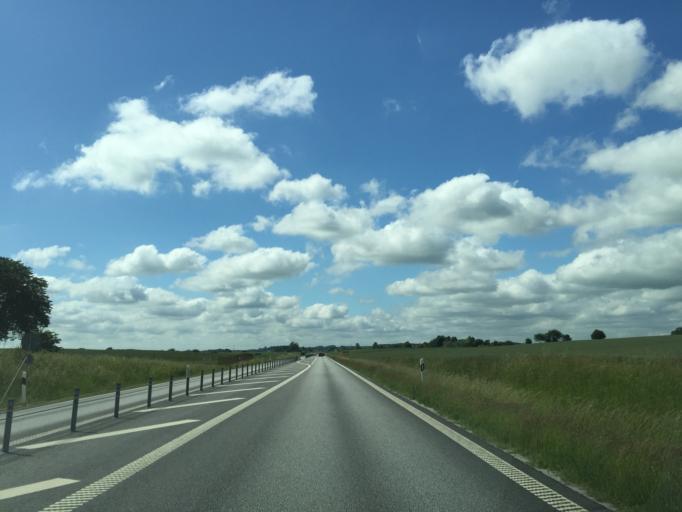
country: SE
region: Skane
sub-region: Skurups Kommun
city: Rydsgard
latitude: 55.4851
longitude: 13.5708
